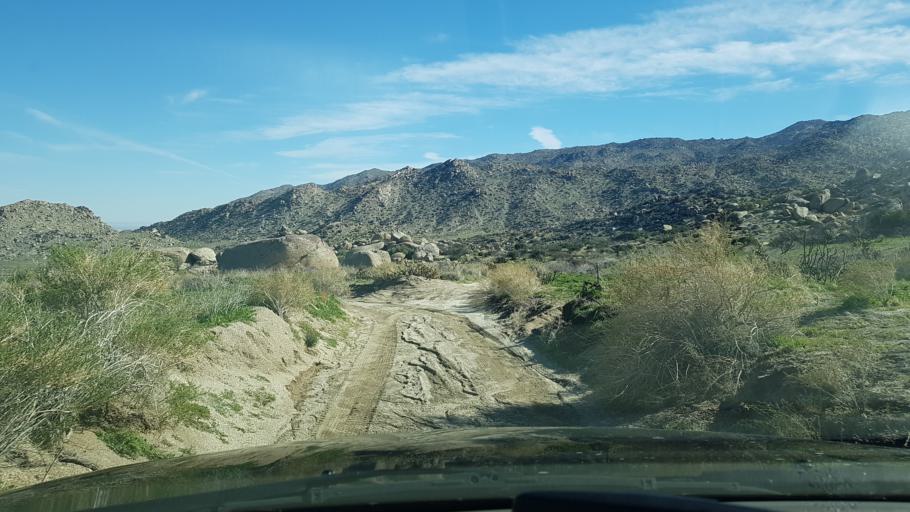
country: US
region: California
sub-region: San Diego County
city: Borrego Springs
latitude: 33.2111
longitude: -116.4602
